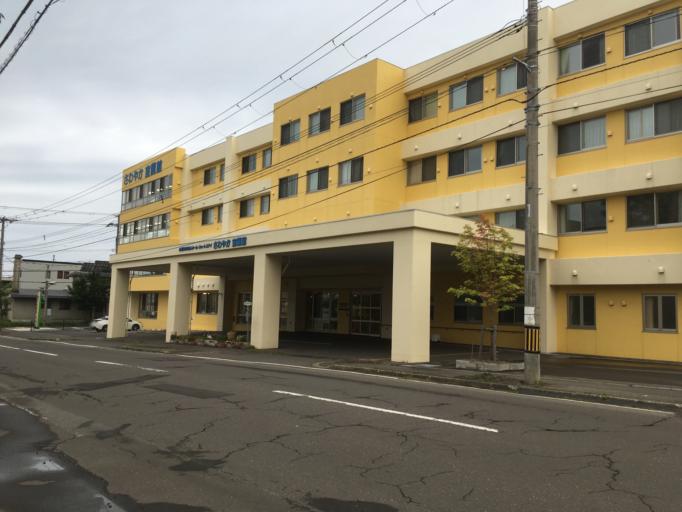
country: JP
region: Hokkaido
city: Muroran
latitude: 42.3157
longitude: 140.9701
